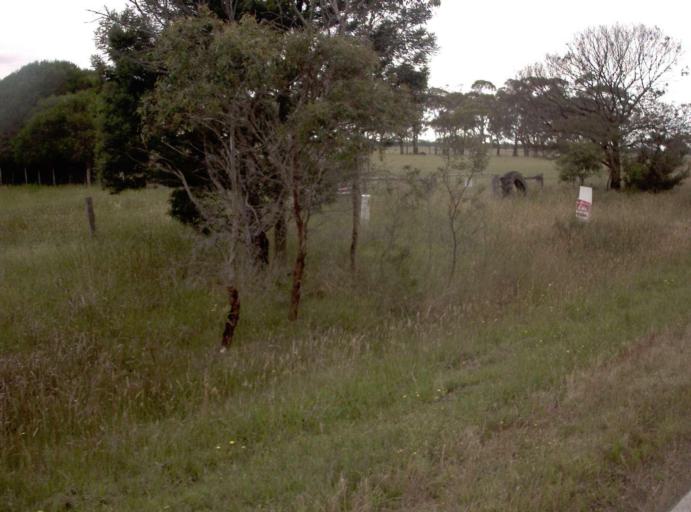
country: AU
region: Victoria
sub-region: Latrobe
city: Traralgon
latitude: -38.5543
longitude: 146.7607
